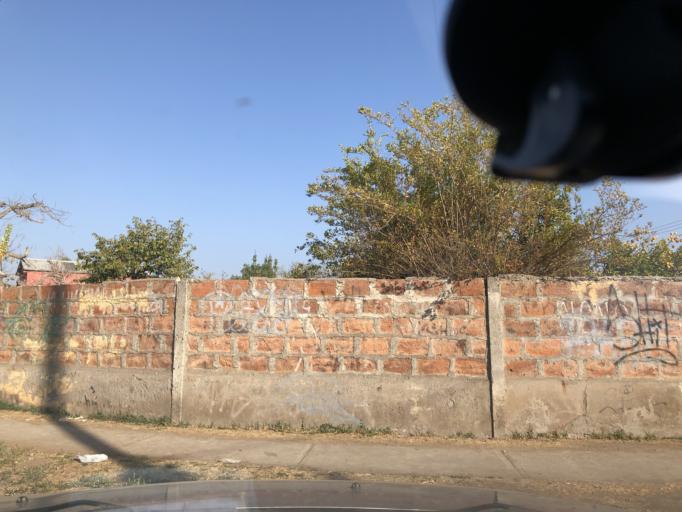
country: CL
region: Santiago Metropolitan
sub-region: Provincia de Cordillera
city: Puente Alto
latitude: -33.6225
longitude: -70.5783
